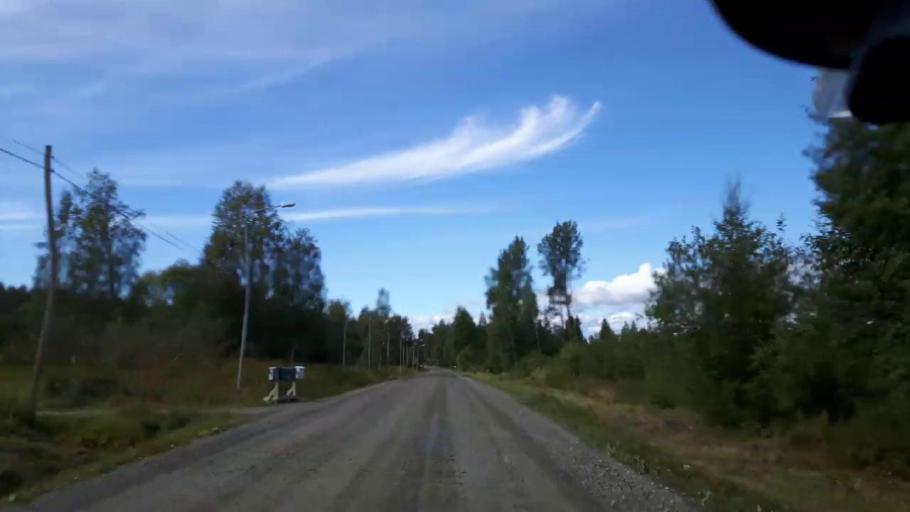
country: SE
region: Jaemtland
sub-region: Ragunda Kommun
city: Hammarstrand
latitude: 63.1432
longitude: 15.9048
